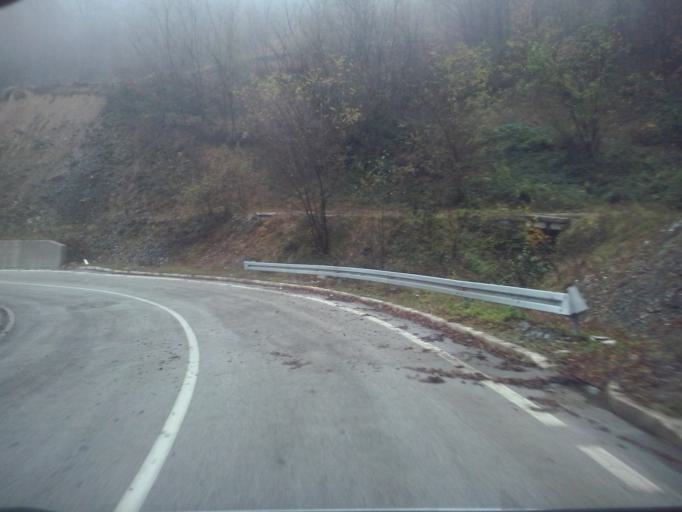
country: RS
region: Central Serbia
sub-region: Moravicki Okrug
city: Ivanjica
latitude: 43.5366
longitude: 20.2983
